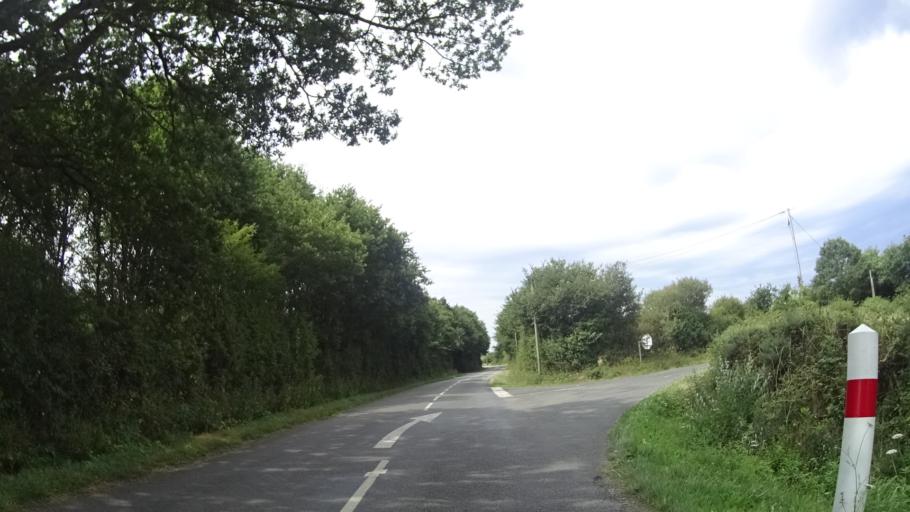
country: FR
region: Pays de la Loire
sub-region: Departement de la Loire-Atlantique
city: Heric
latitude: 47.4483
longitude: -1.7063
